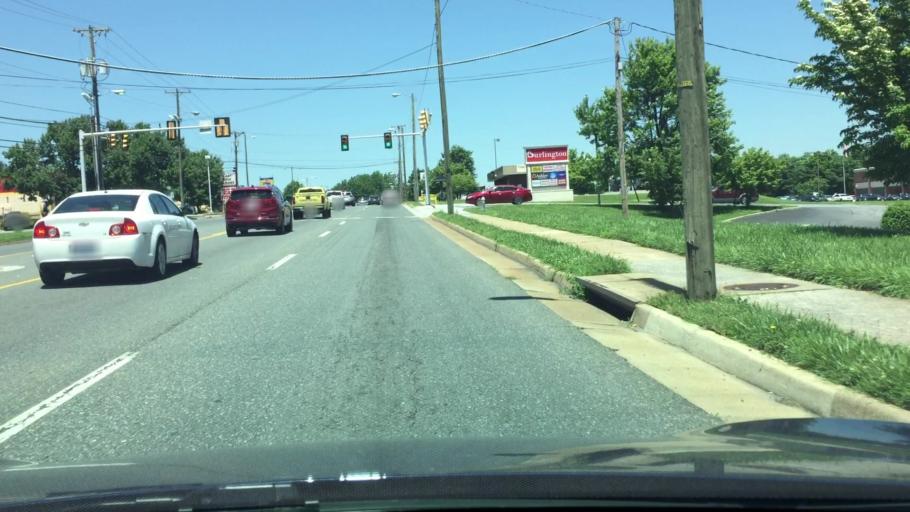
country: US
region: Virginia
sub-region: City of Lynchburg
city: West Lynchburg
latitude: 37.3729
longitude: -79.1844
